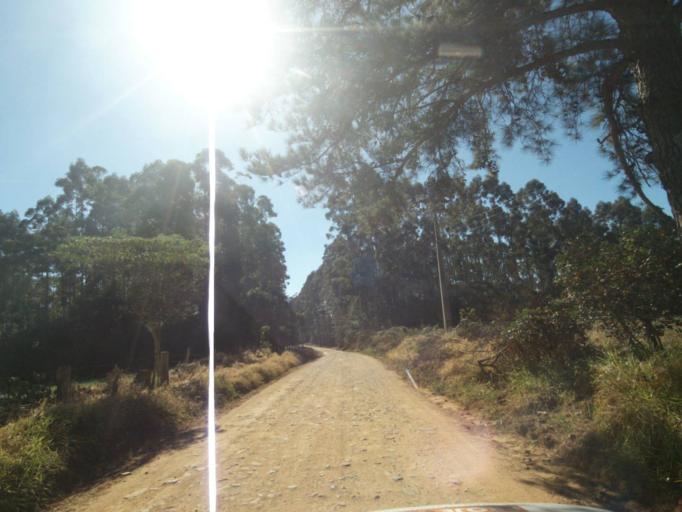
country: BR
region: Parana
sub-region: Tibagi
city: Tibagi
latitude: -24.5557
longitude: -50.6214
